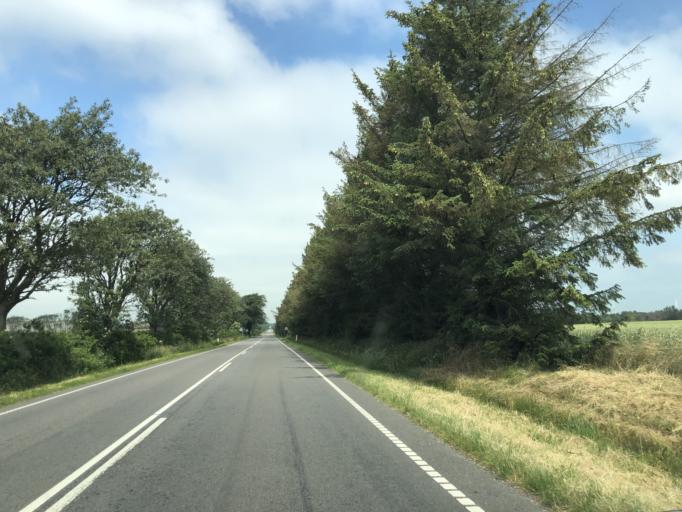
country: DK
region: South Denmark
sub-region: Varde Kommune
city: Varde
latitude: 55.6619
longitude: 8.4900
